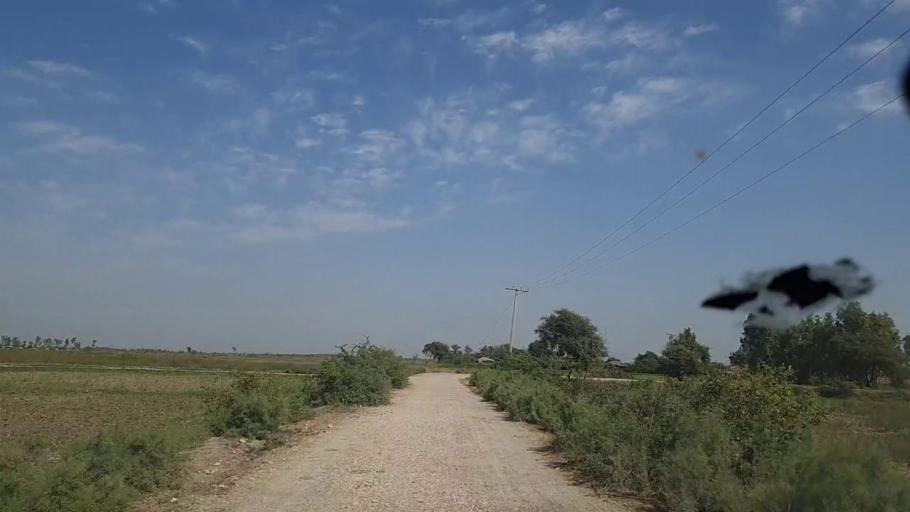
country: PK
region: Sindh
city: Daro Mehar
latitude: 24.6633
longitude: 68.0831
